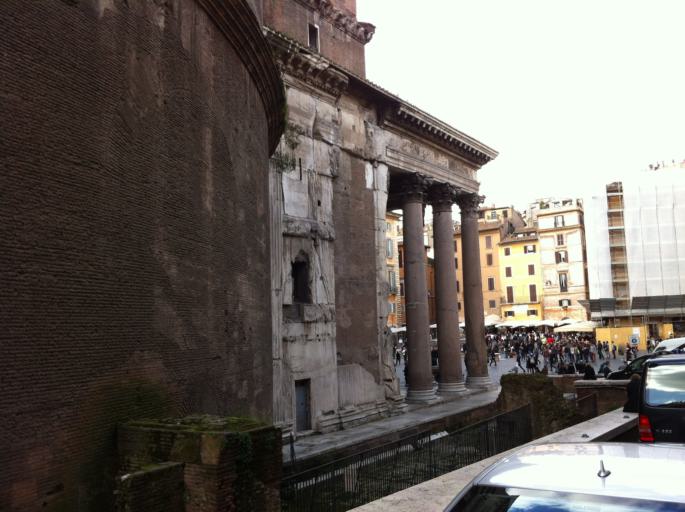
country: VA
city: Vatican City
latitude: 41.8986
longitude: 12.4773
